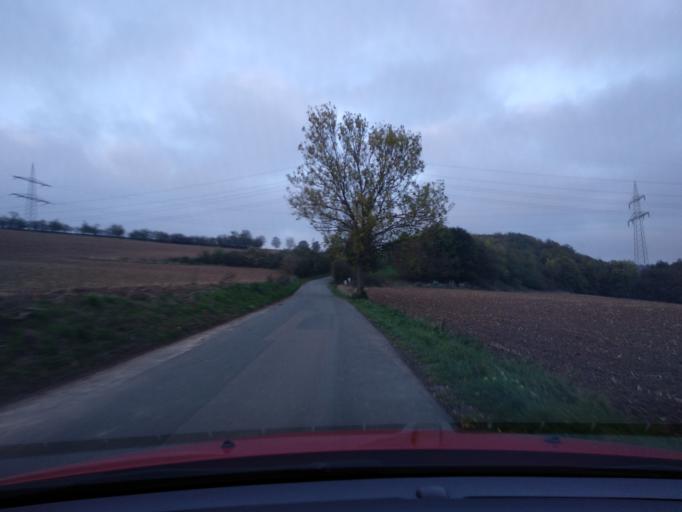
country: DE
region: North Rhine-Westphalia
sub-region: Regierungsbezirk Detmold
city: Paderborn
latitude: 51.6662
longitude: 8.7427
